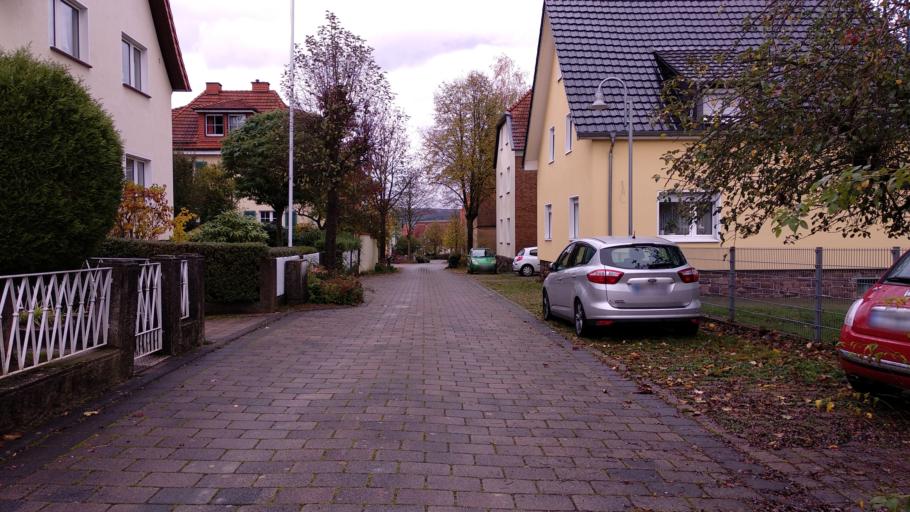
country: DE
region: North Rhine-Westphalia
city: Beverungen
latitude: 51.6624
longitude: 9.3665
